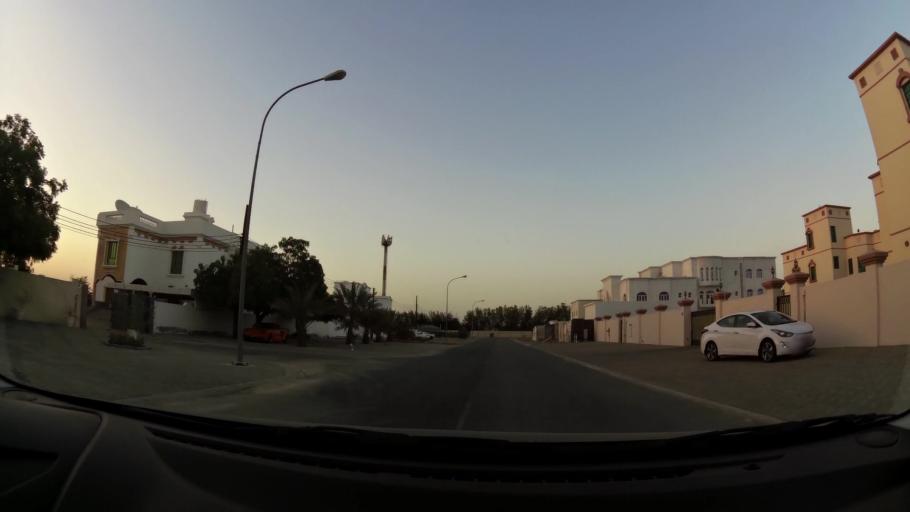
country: OM
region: Muhafazat Masqat
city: As Sib al Jadidah
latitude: 23.6463
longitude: 58.2091
